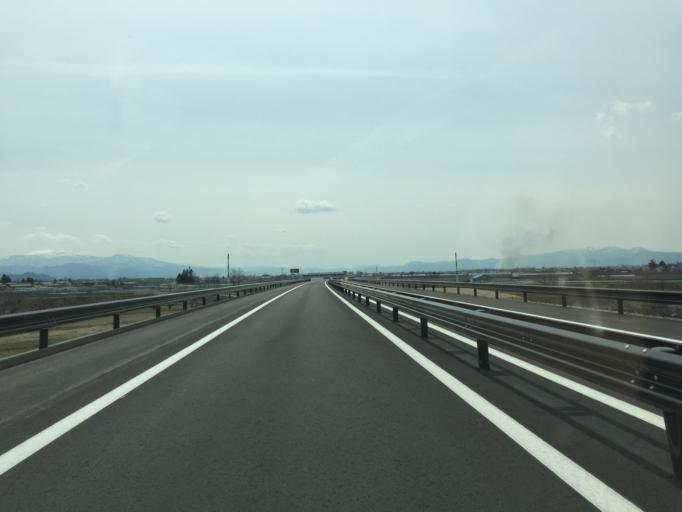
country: JP
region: Yamagata
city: Higashine
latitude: 38.4251
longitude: 140.3524
